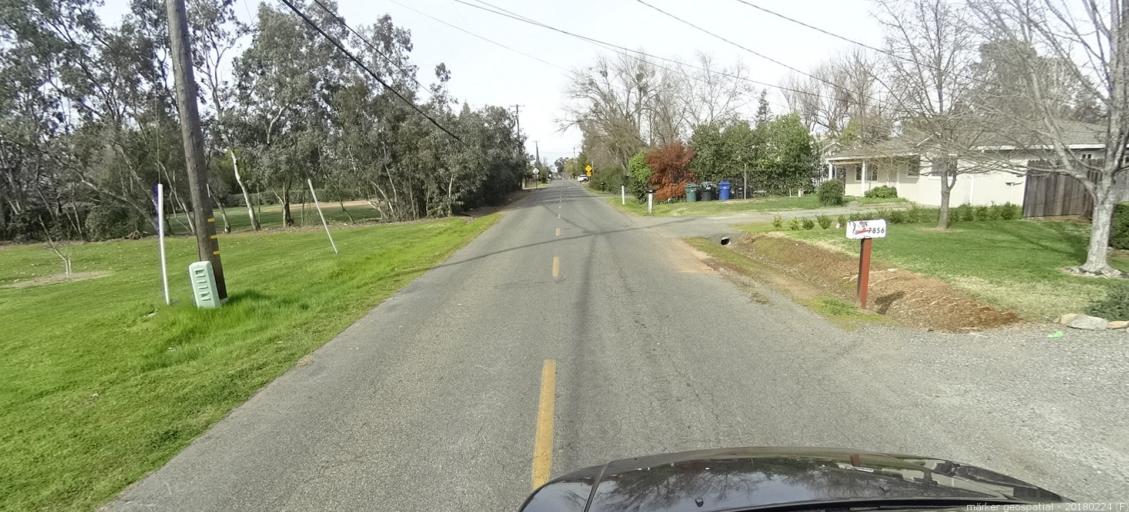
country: US
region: California
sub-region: Sacramento County
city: Elverta
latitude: 38.7119
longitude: -121.4512
